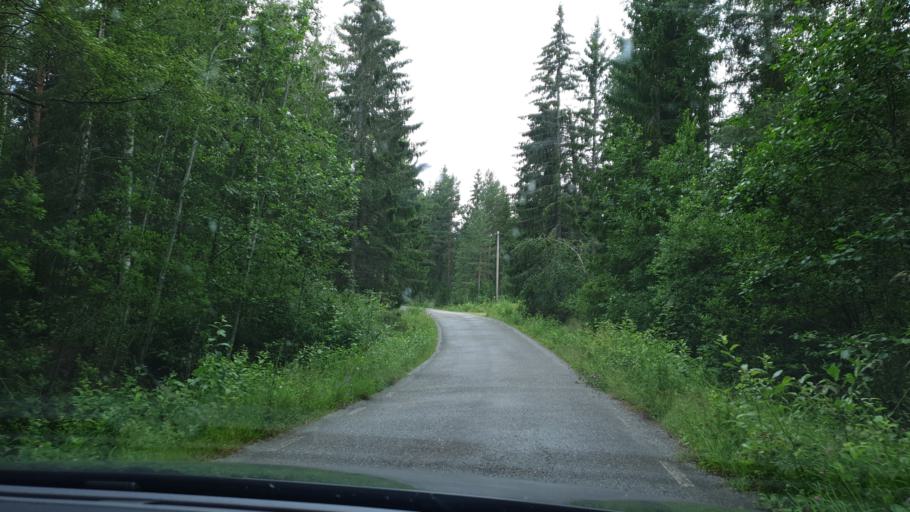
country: SE
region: Gaevleborg
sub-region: Hudiksvalls Kommun
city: Iggesund
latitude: 61.5369
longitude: 17.0105
